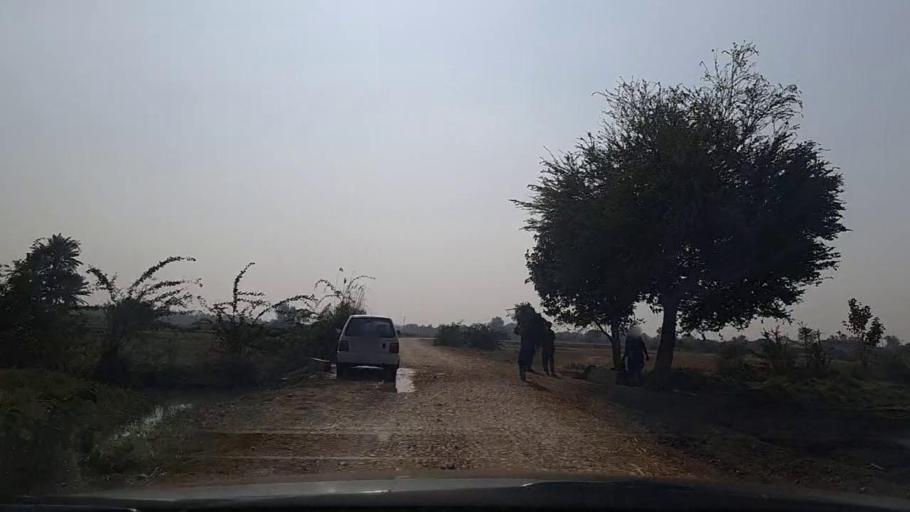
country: PK
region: Sindh
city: Mirpur Sakro
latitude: 24.5654
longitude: 67.7776
